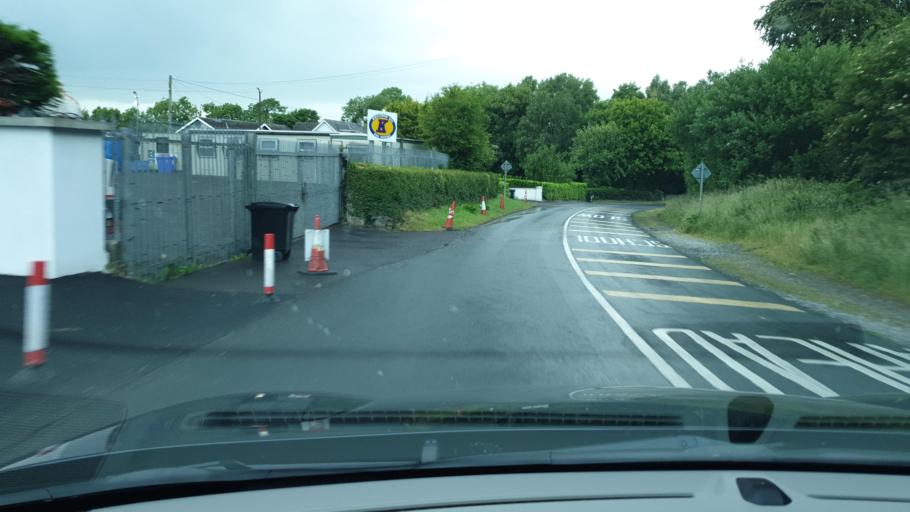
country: IE
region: Leinster
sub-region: An Mhi
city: Navan
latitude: 53.6222
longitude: -6.6673
